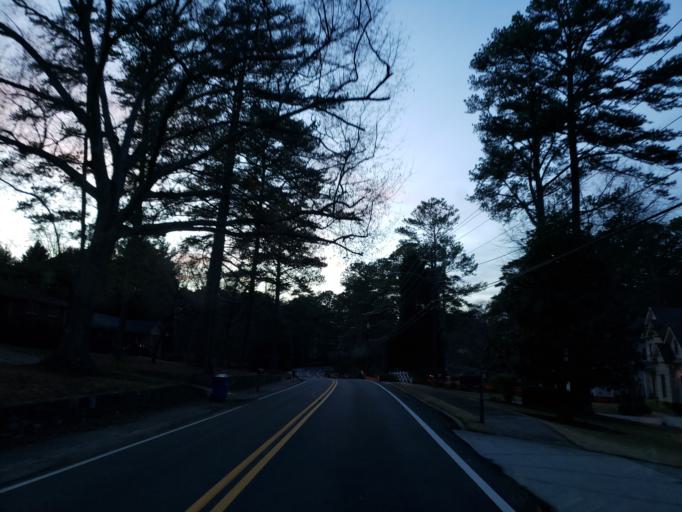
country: US
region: Georgia
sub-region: DeKalb County
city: Scottdale
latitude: 33.8265
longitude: -84.2756
